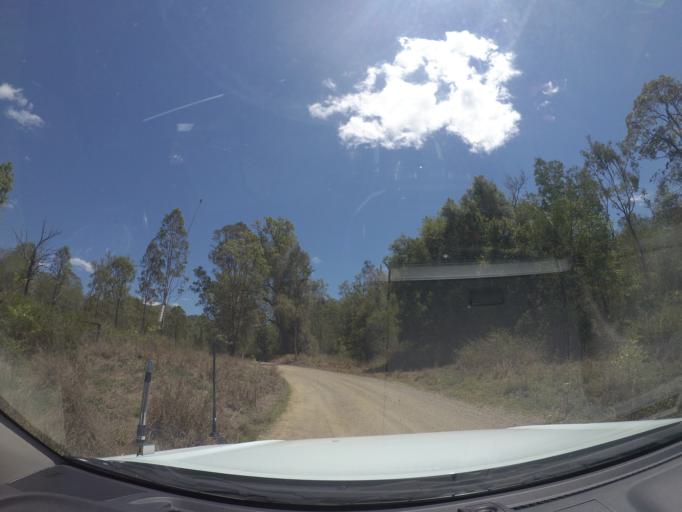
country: AU
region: Queensland
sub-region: Ipswich
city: Springfield Lakes
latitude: -27.8110
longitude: 152.8506
